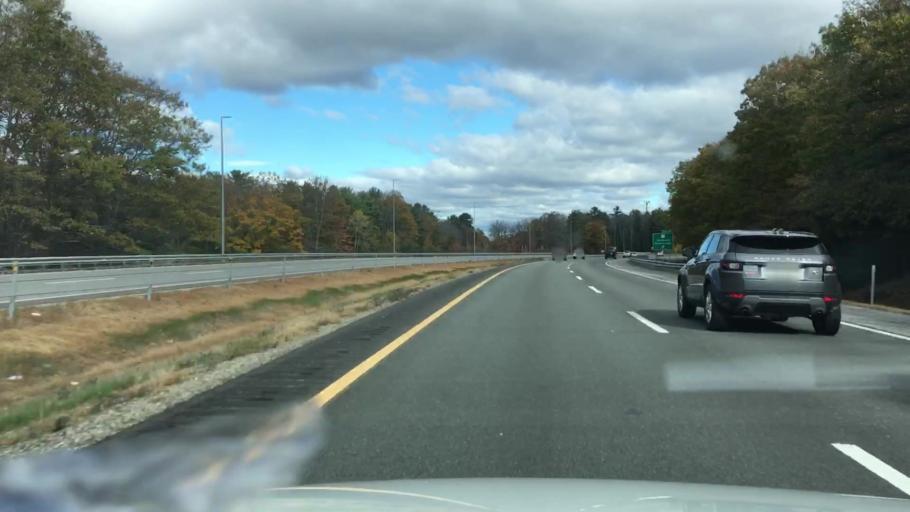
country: US
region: Maine
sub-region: Cumberland County
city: Yarmouth
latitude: 43.7806
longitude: -70.1955
